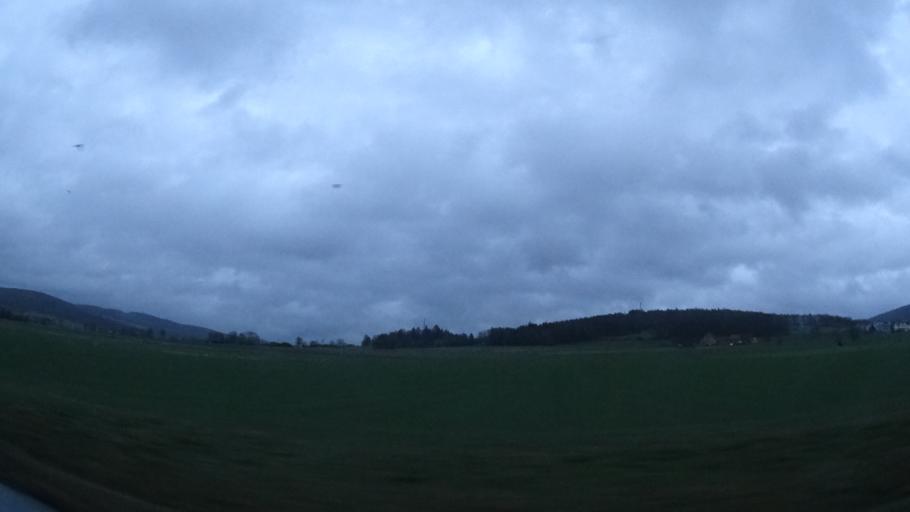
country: DE
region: Bavaria
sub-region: Regierungsbezirk Unterfranken
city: Motten
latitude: 50.4454
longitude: 9.7756
